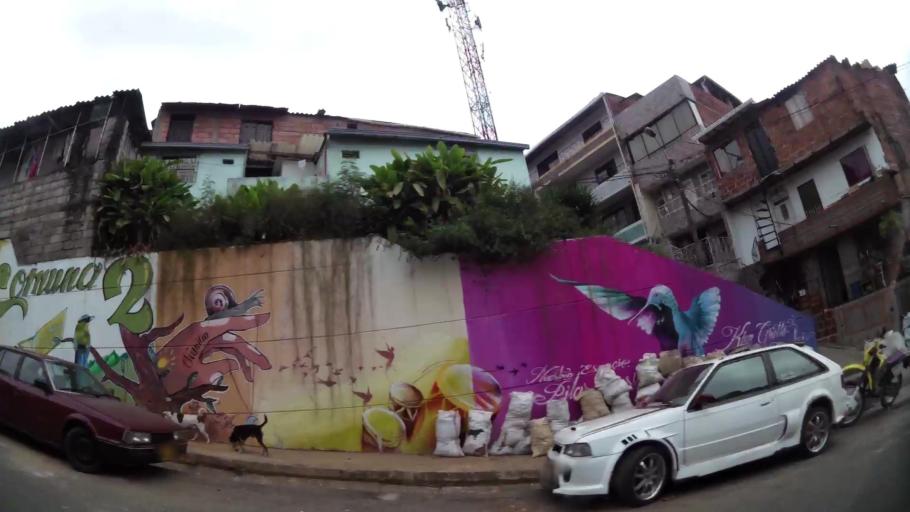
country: CO
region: Antioquia
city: Bello
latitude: 6.2953
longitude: -75.5549
